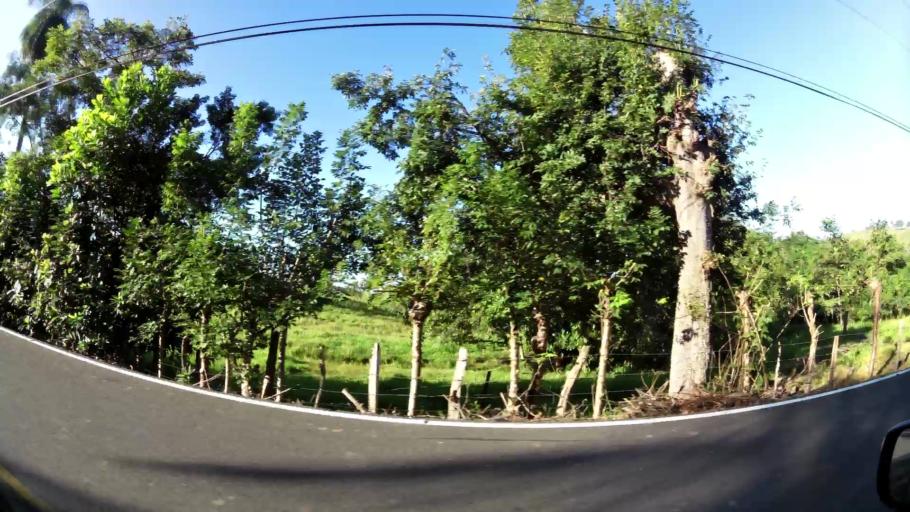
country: CR
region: Puntarenas
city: Miramar
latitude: 10.1593
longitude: -84.8529
